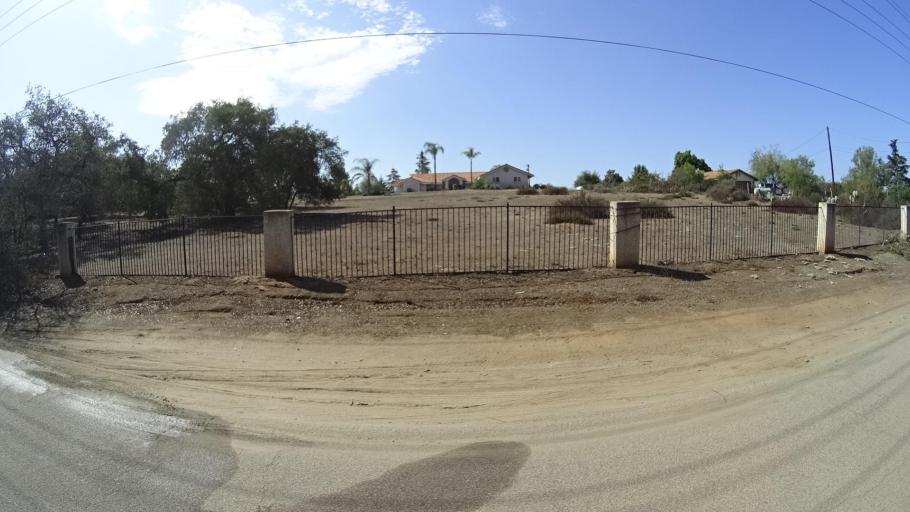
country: US
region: California
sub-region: San Diego County
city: Valley Center
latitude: 33.2856
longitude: -117.0221
